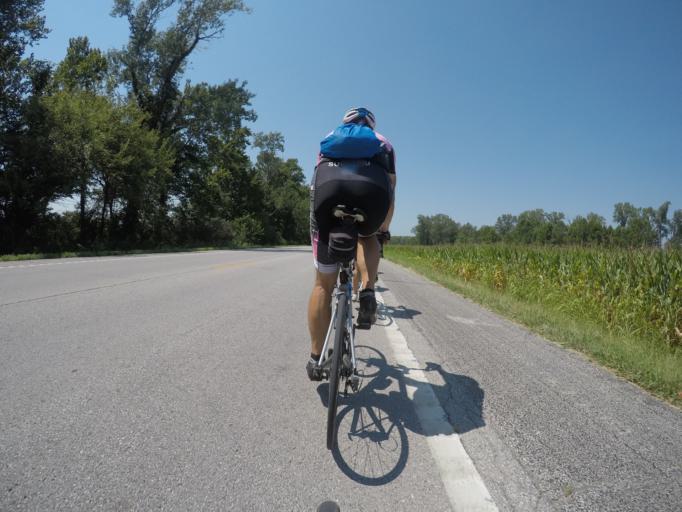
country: US
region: Kansas
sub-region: Leavenworth County
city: Leavenworth
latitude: 39.3277
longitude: -94.8792
